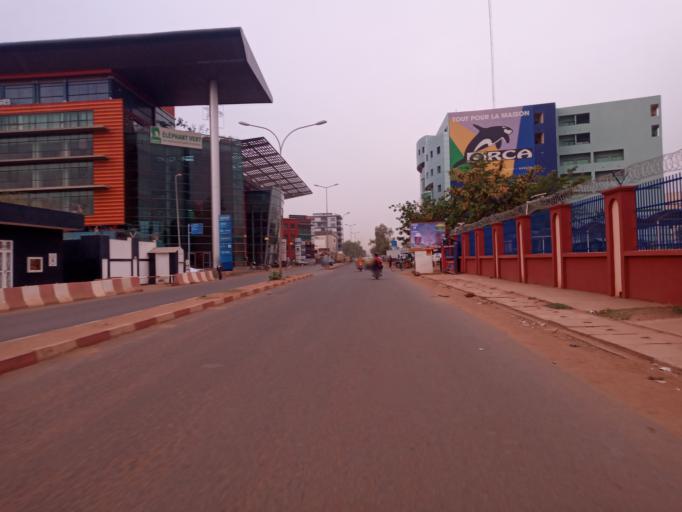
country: ML
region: Bamako
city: Bamako
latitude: 12.6335
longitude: -8.0270
